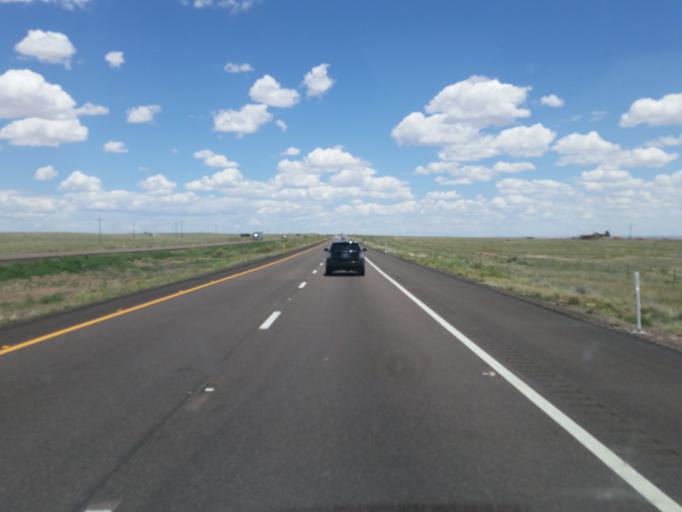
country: US
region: Arizona
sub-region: Navajo County
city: Holbrook
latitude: 34.9840
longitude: -110.0354
